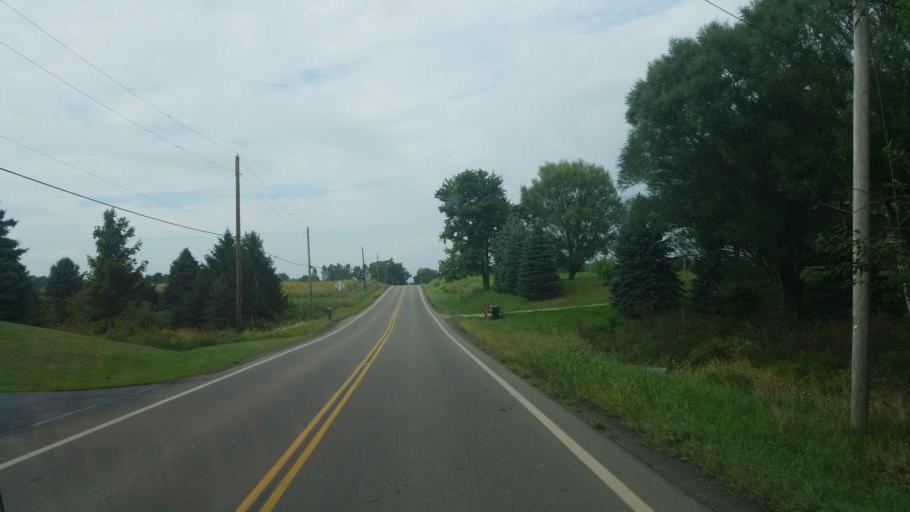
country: US
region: Ohio
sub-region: Wayne County
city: West Salem
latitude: 40.9169
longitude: -82.0517
